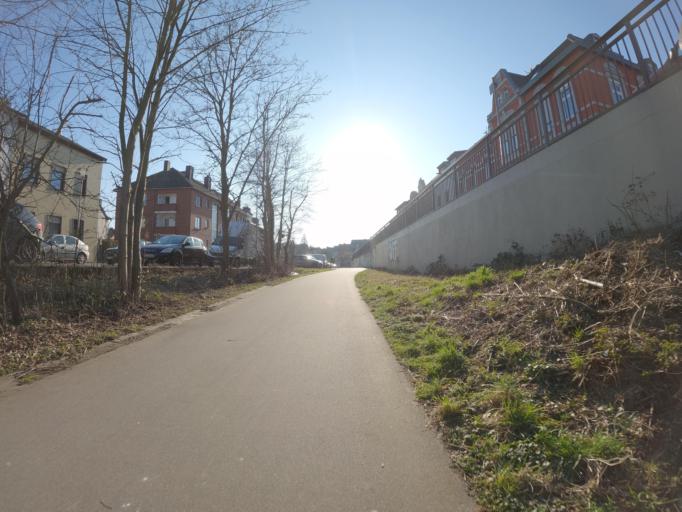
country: DE
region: North Rhine-Westphalia
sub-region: Regierungsbezirk Koln
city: Wurselen
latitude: 50.8193
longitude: 6.1354
